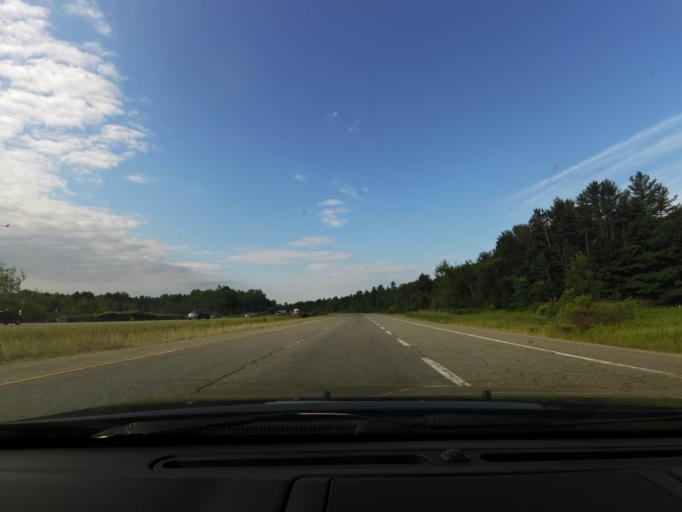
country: CA
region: Ontario
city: Gravenhurst
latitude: 44.9370
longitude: -79.3425
